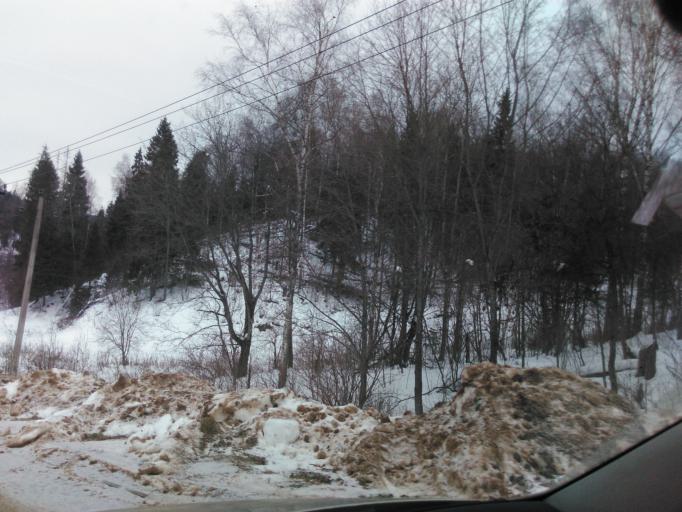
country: RU
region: Moskovskaya
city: Podosinki
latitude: 56.2721
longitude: 37.6197
